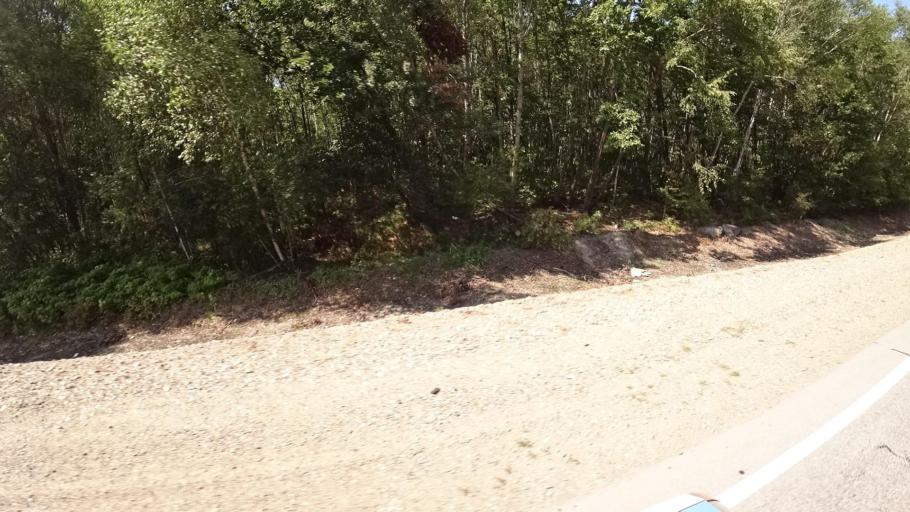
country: RU
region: Khabarovsk Krai
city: Khor
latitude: 47.9833
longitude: 135.0880
